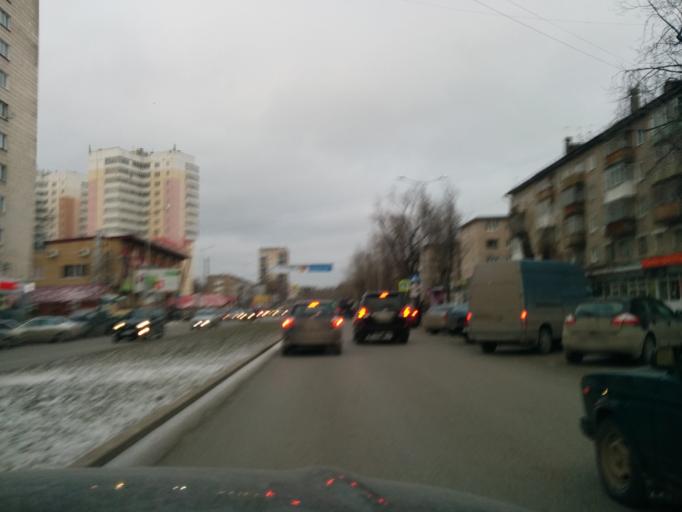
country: RU
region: Perm
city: Kultayevo
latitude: 58.0048
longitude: 55.9508
